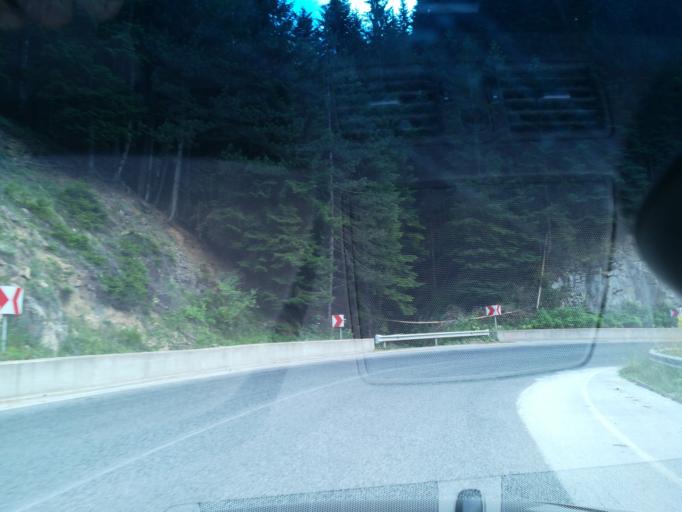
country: BG
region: Smolyan
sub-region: Obshtina Chepelare
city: Chepelare
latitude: 41.6763
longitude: 24.7584
